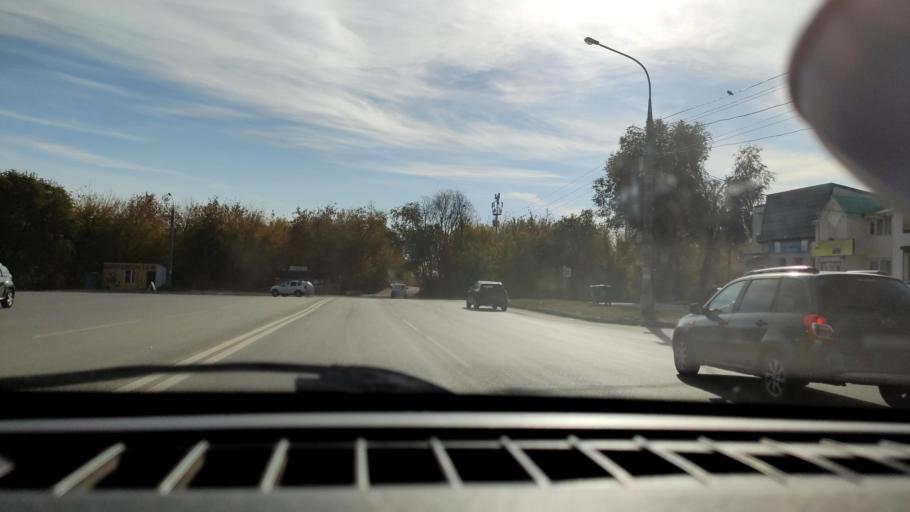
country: RU
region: Samara
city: Samara
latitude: 53.2259
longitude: 50.2107
